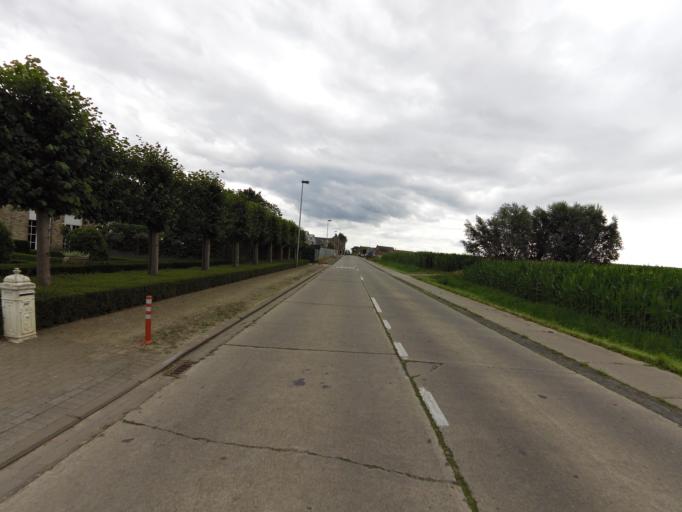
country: BE
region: Flanders
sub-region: Provincie West-Vlaanderen
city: Staden
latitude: 50.9921
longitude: 3.0339
